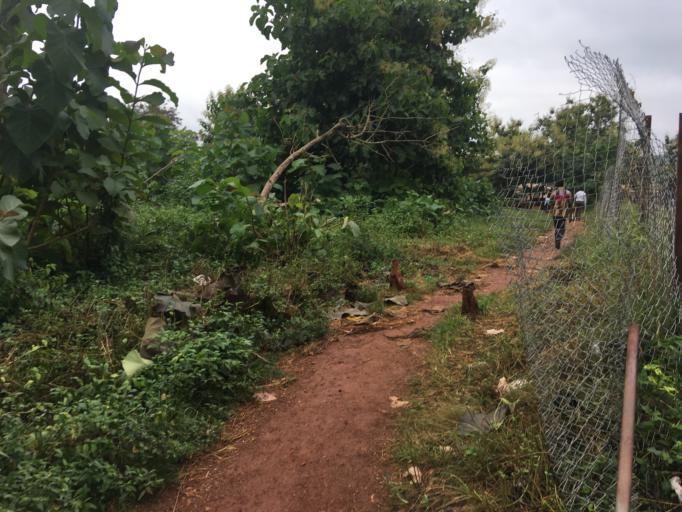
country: GH
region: Western
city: Bibiani
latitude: 6.8006
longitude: -2.5185
